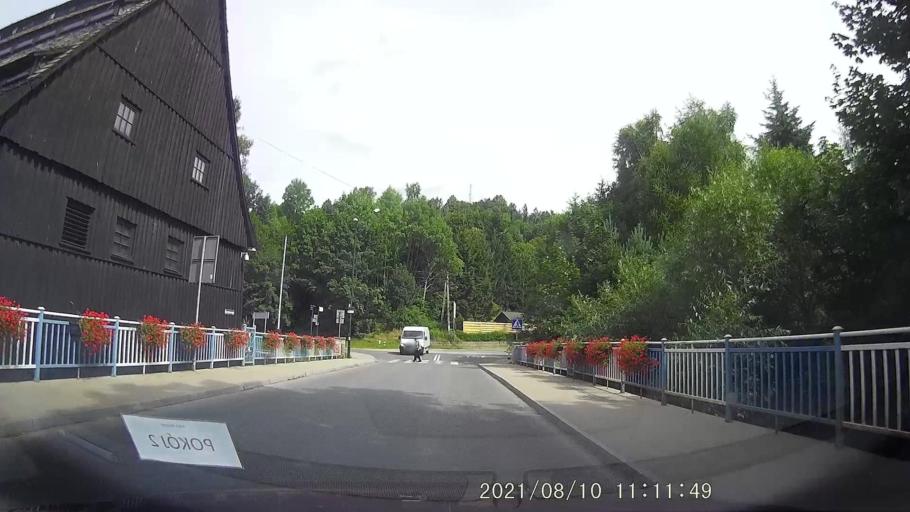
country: PL
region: Lower Silesian Voivodeship
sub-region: Powiat klodzki
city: Duszniki-Zdroj
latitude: 50.4057
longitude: 16.3981
